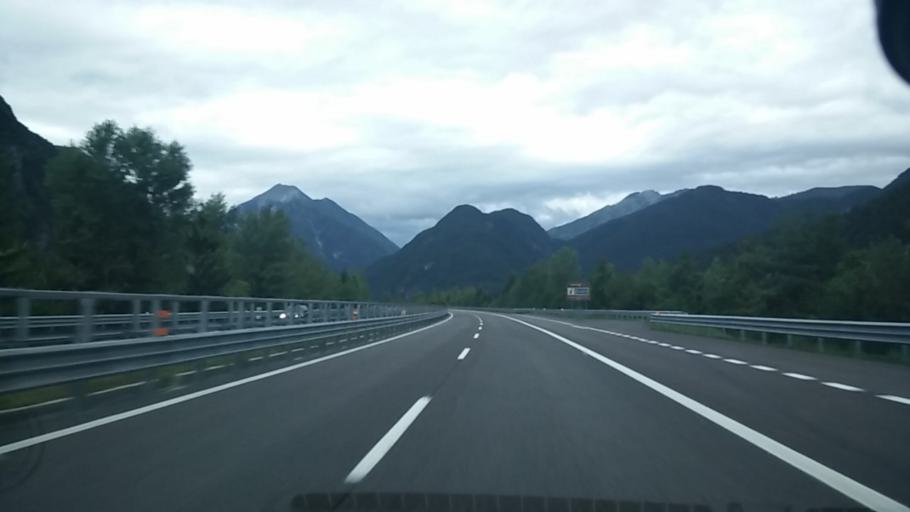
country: IT
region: Friuli Venezia Giulia
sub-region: Provincia di Udine
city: Resiutta
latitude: 46.3964
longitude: 13.2166
